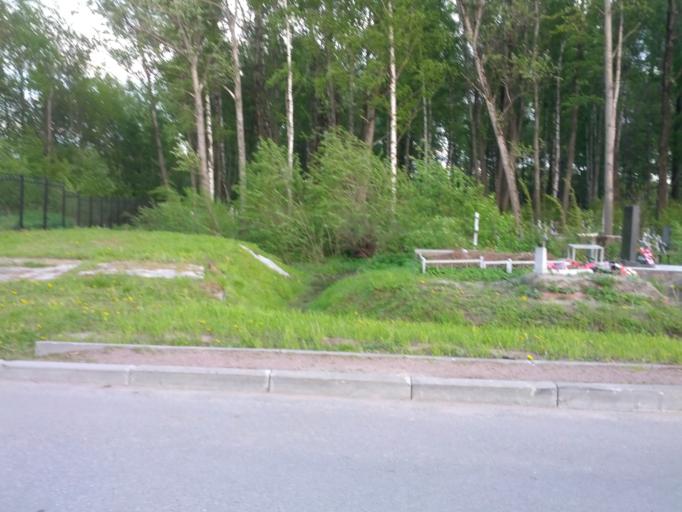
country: RU
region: St.-Petersburg
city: Obukhovo
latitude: 59.9133
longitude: 30.4334
